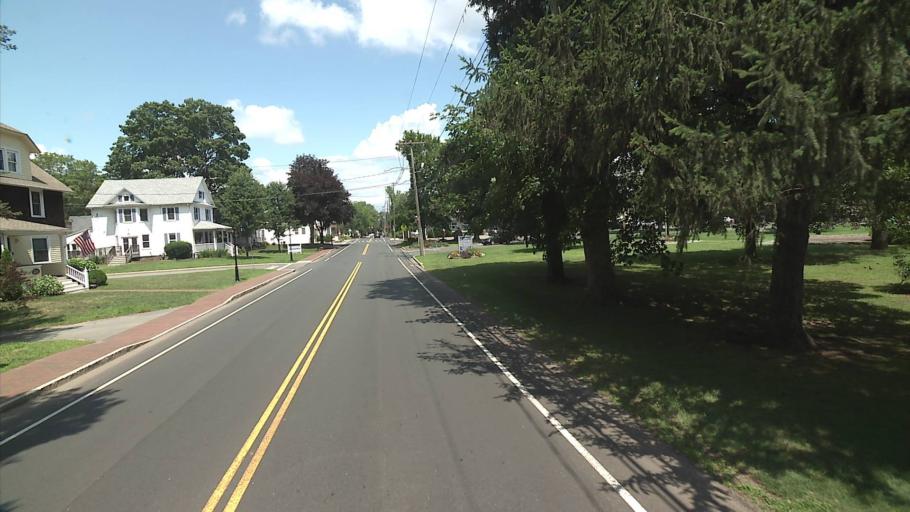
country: US
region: Connecticut
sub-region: Middlesex County
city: Deep River Center
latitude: 41.3831
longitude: -72.4350
